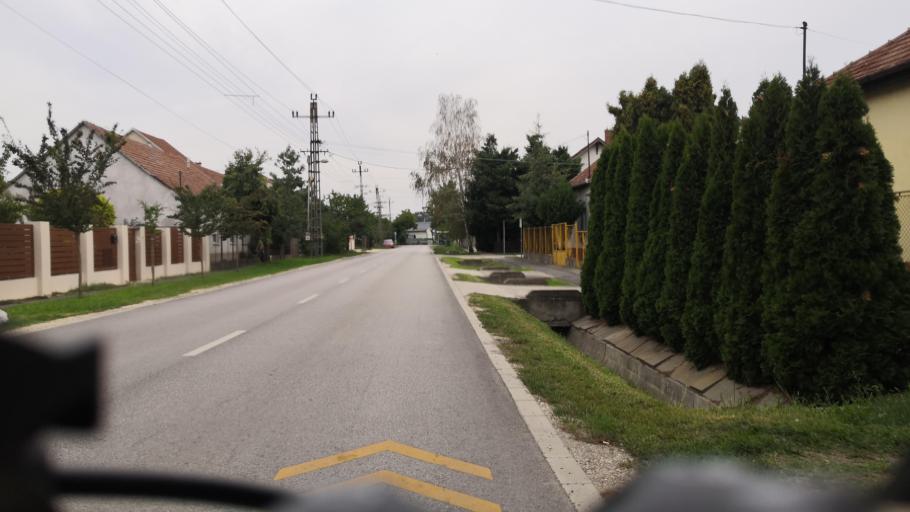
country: HU
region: Csongrad
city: Szeged
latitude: 46.2823
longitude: 20.1660
